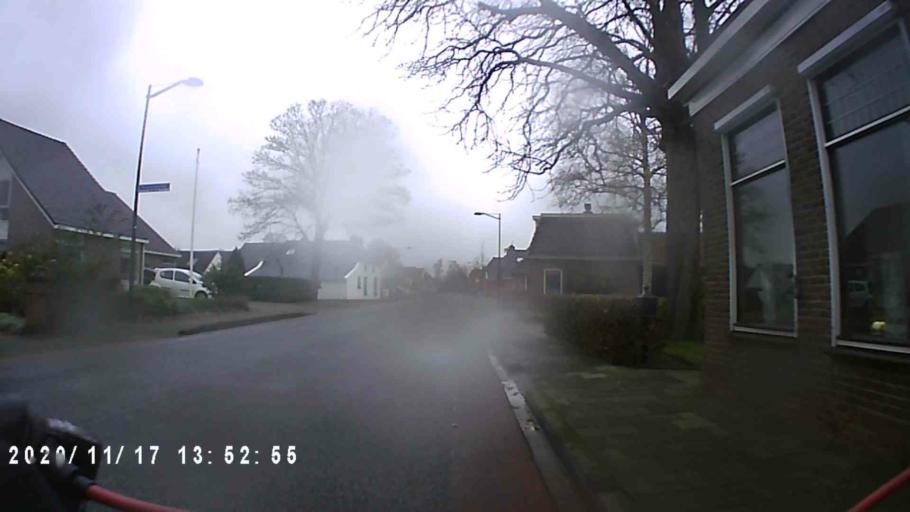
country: NL
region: Groningen
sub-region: Gemeente Zuidhorn
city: Zuidhorn
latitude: 53.2284
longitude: 6.3568
